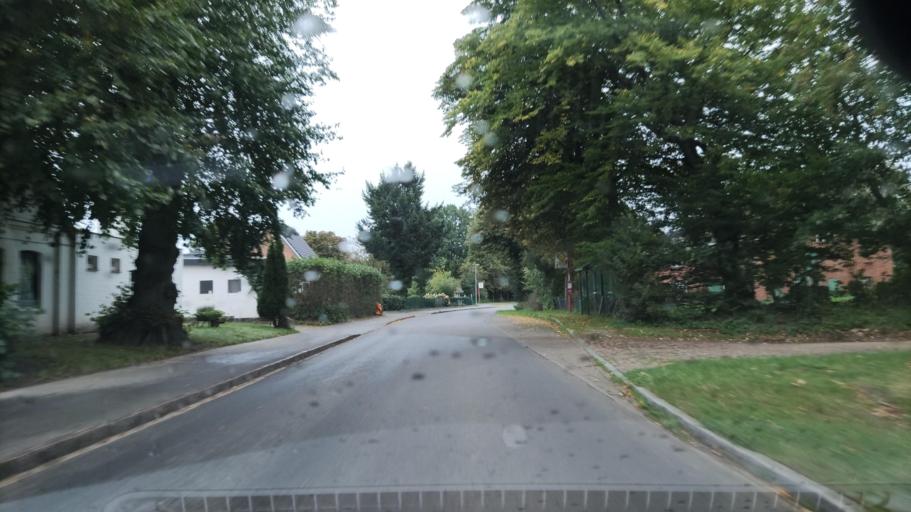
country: DE
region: Schleswig-Holstein
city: Grande
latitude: 53.5957
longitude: 10.3750
